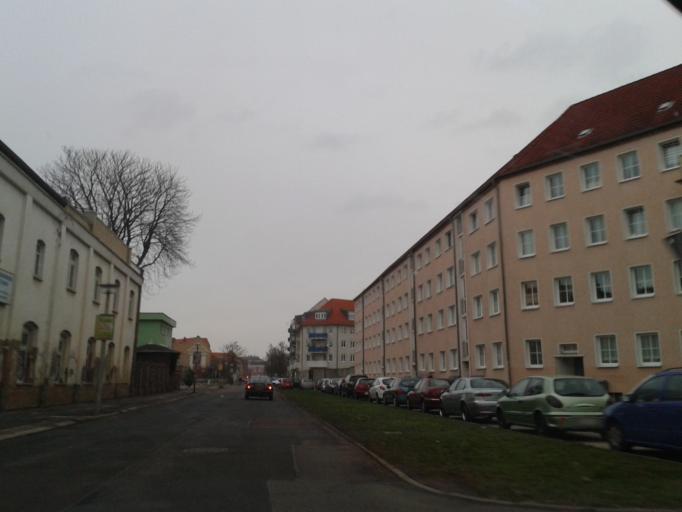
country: DE
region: Saxony-Anhalt
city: Halle (Saale)
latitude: 51.4679
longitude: 11.9782
